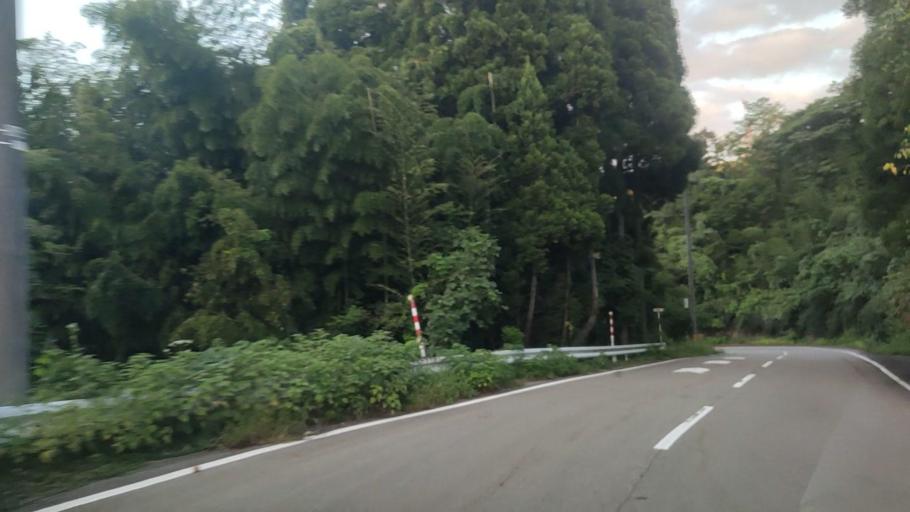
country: JP
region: Ishikawa
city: Tsubata
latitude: 36.6304
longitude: 136.7736
